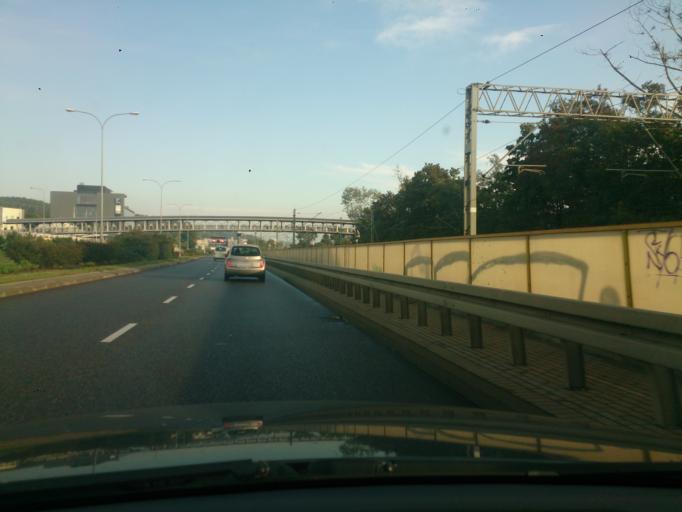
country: PL
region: Pomeranian Voivodeship
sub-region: Gdynia
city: Gdynia
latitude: 54.4951
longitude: 18.5362
